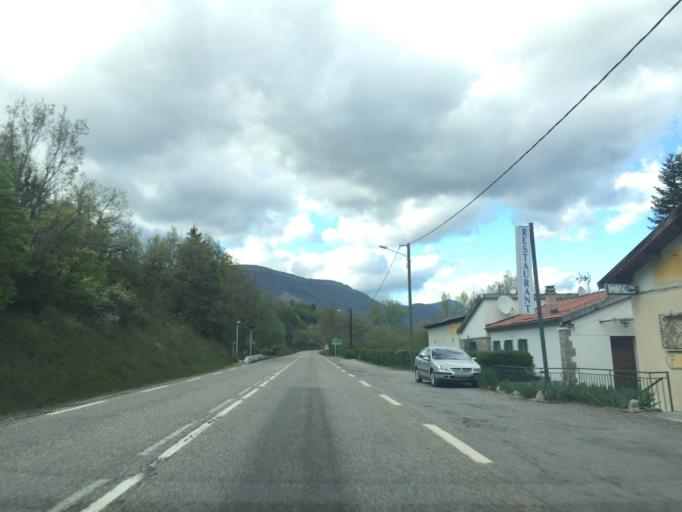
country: FR
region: Provence-Alpes-Cote d'Azur
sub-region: Departement des Hautes-Alpes
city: Serres
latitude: 44.4971
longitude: 5.7297
